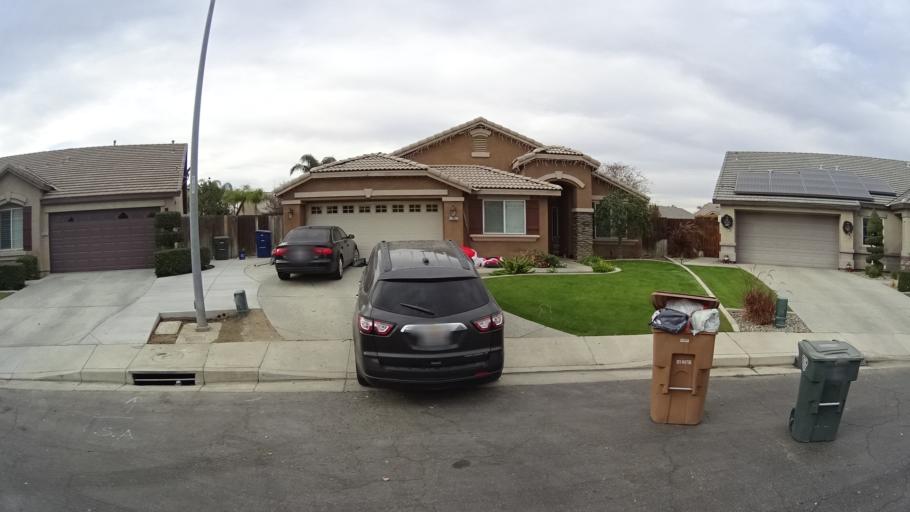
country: US
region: California
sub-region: Kern County
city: Rosedale
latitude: 35.4067
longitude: -119.1469
